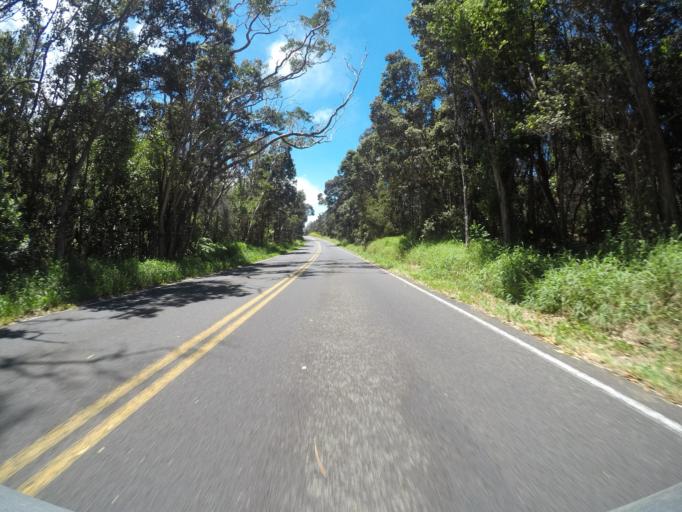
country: US
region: Hawaii
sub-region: Hawaii County
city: Volcano
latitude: 19.3944
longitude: -155.2512
